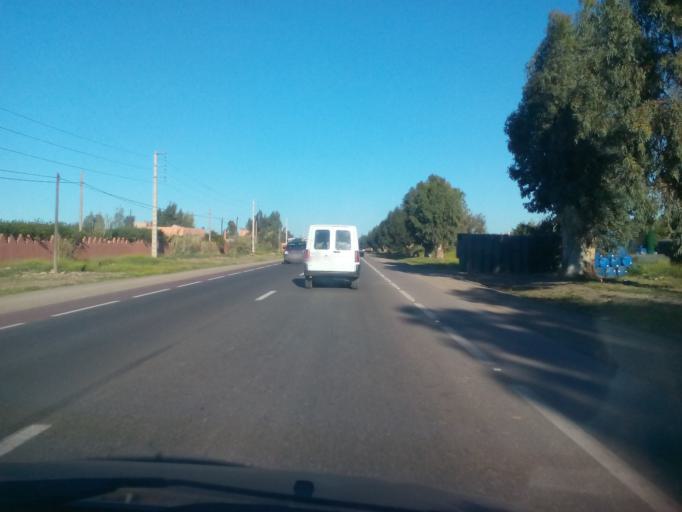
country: MA
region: Marrakech-Tensift-Al Haouz
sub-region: Marrakech
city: Marrakesh
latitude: 31.6319
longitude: -8.1940
